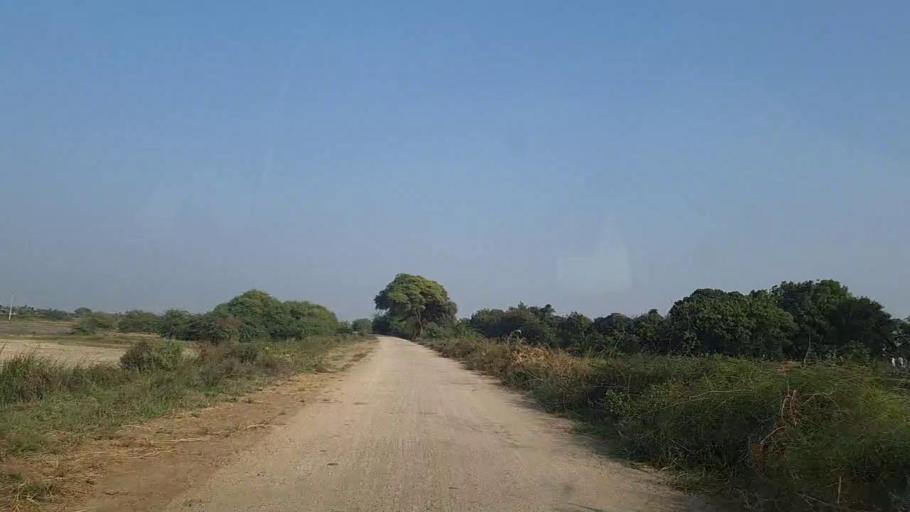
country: PK
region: Sindh
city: Mirpur Sakro
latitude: 24.5745
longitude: 67.6801
